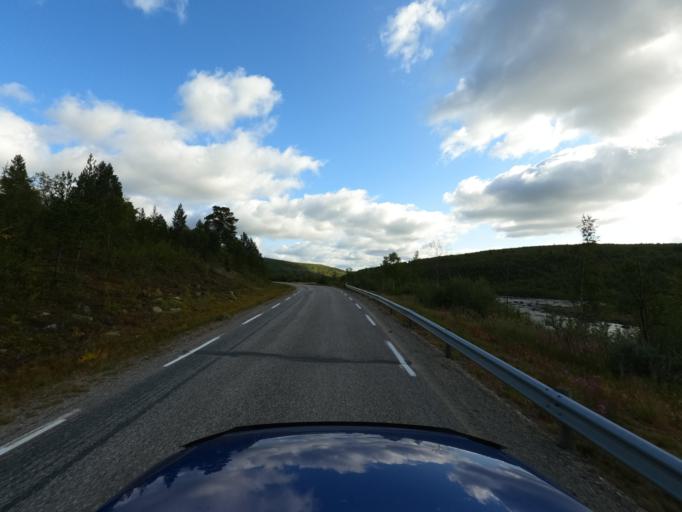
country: NO
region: Finnmark Fylke
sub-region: Porsanger
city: Lakselv
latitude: 69.4271
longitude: 24.8711
